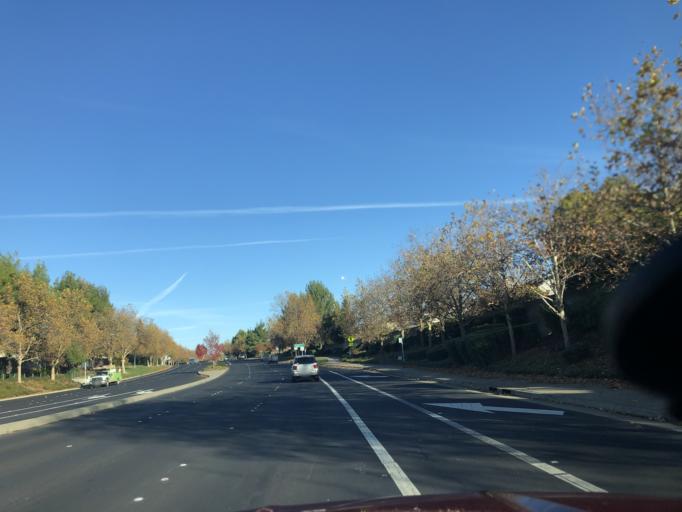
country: US
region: California
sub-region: Placer County
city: Roseville
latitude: 38.7738
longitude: -121.3033
